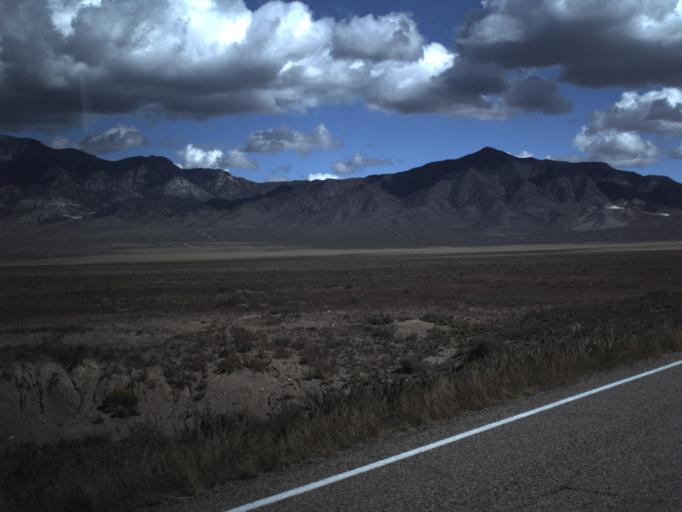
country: US
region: Utah
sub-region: Beaver County
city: Milford
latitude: 38.4633
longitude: -113.3850
